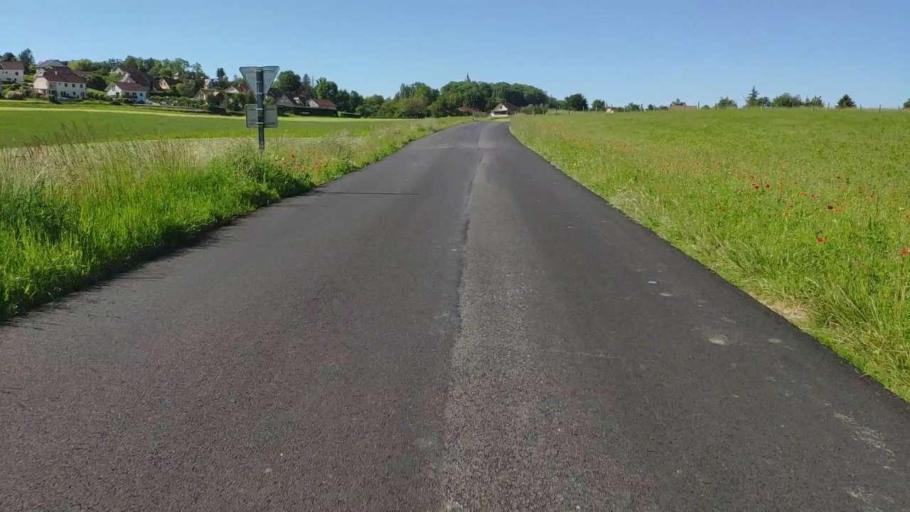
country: FR
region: Franche-Comte
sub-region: Departement du Jura
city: Perrigny
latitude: 46.7143
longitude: 5.5832
